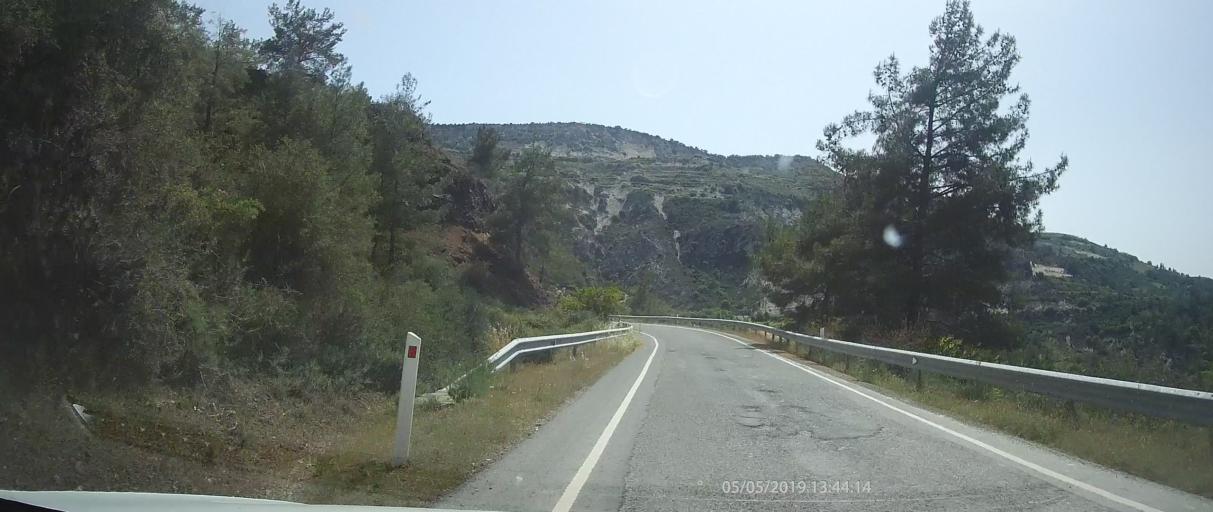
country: CY
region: Limassol
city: Pachna
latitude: 34.8714
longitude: 32.7913
